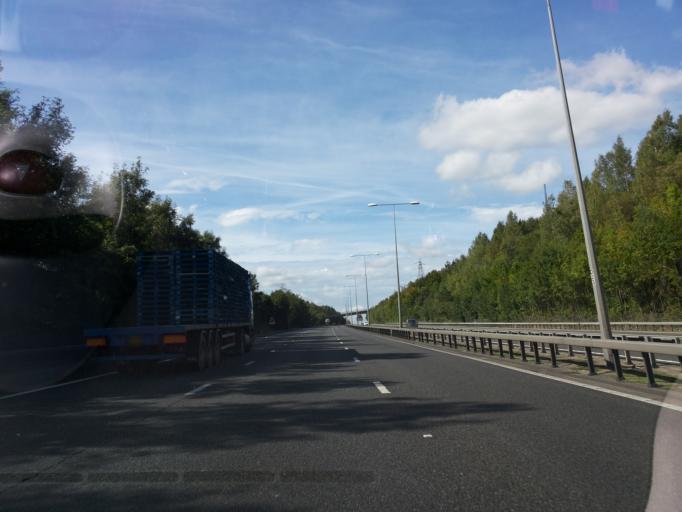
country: GB
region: England
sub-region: Kent
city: Borough Green
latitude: 51.3158
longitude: 0.2966
